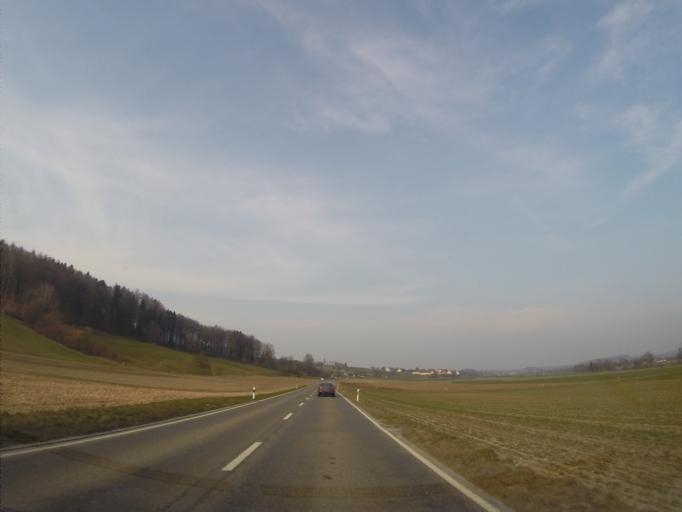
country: CH
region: Zurich
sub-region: Bezirk Winterthur
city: Neftenbach / Dorf Neftenbach
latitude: 47.5341
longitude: 8.6693
